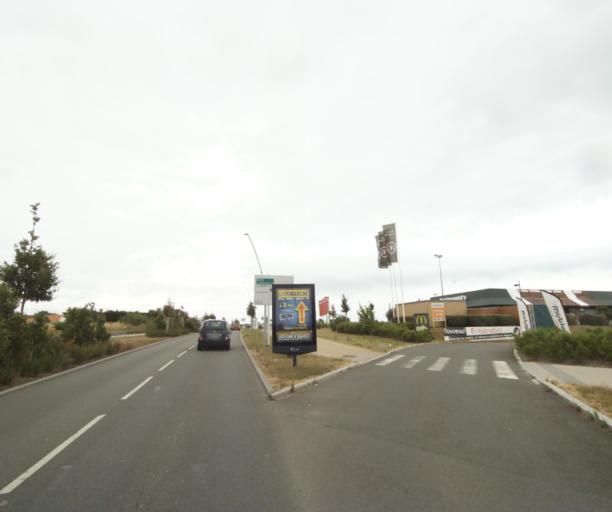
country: FR
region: Pays de la Loire
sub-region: Departement de la Vendee
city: Chateau-d'Olonne
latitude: 46.4887
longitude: -1.7481
